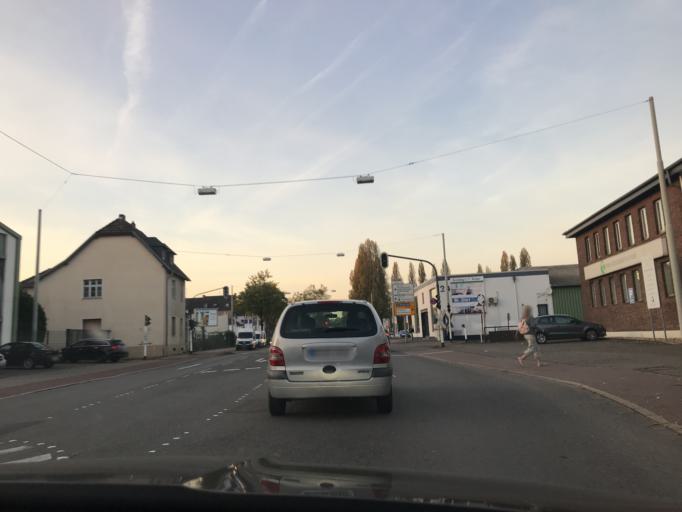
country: DE
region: North Rhine-Westphalia
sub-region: Regierungsbezirk Dusseldorf
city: Krefeld
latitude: 51.3316
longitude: 6.5880
